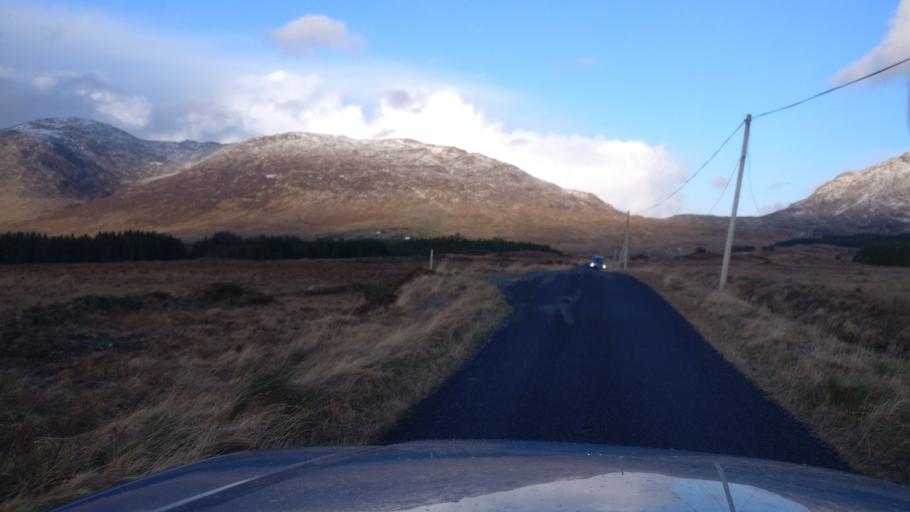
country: IE
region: Connaught
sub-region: County Galway
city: Clifden
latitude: 53.4761
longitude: -9.6860
